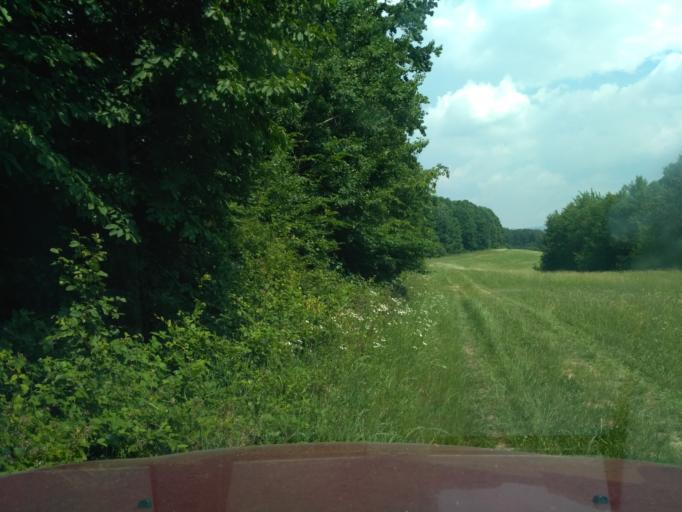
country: SK
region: Kosicky
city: Moldava nad Bodvou
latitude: 48.6278
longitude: 21.0423
